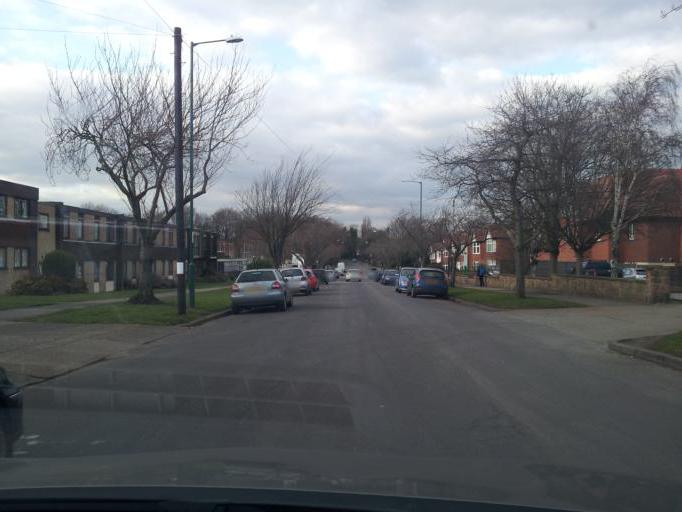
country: GB
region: England
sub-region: Nottingham
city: Nottingham
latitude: 52.9556
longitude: -1.2083
